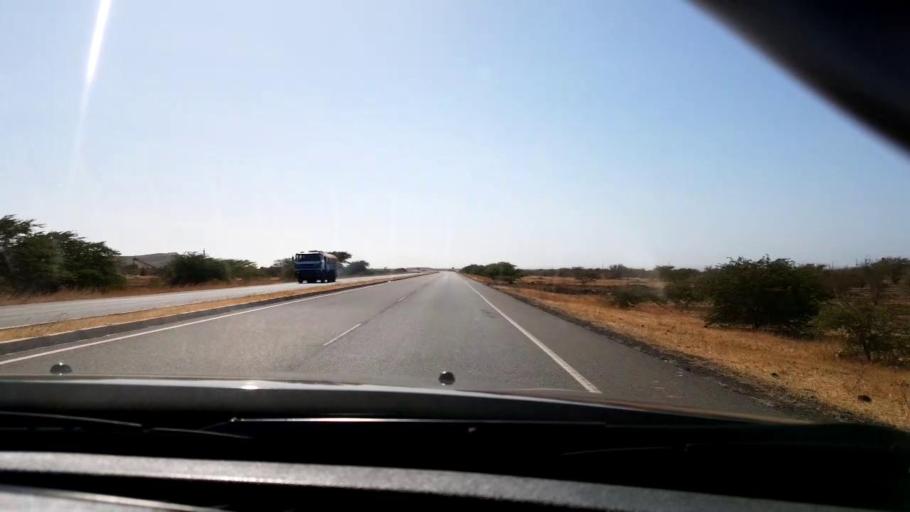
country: CV
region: Praia
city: Praia
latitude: 14.9466
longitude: -23.4903
